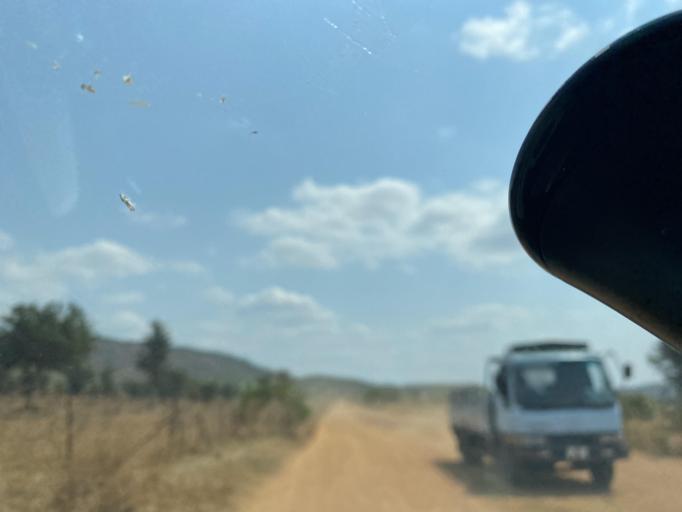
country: ZM
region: Lusaka
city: Chongwe
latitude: -15.5981
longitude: 28.7530
